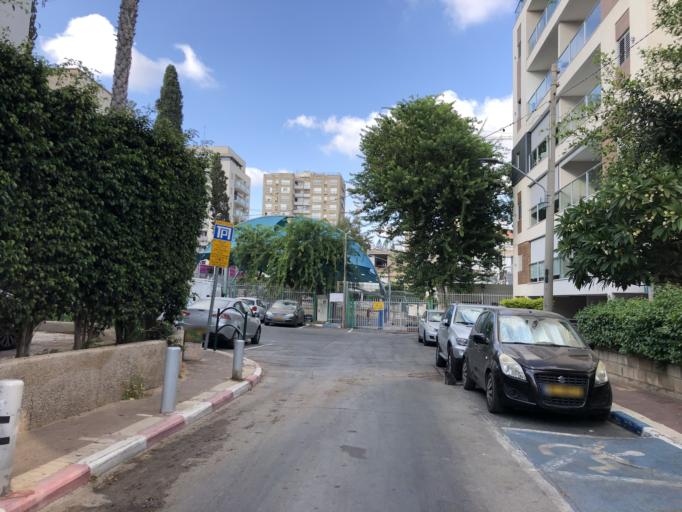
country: IL
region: Tel Aviv
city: Ramat Gan
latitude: 32.0832
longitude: 34.8200
